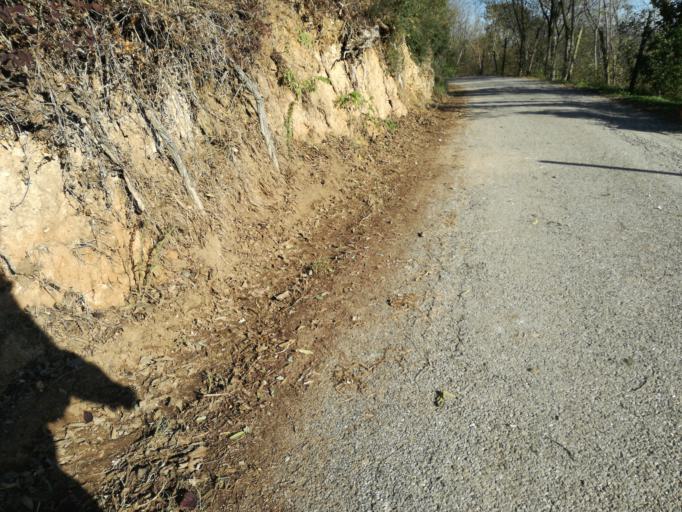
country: IT
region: Veneto
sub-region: Provincia di Padova
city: Arqua Petrarca
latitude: 45.2745
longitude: 11.7329
